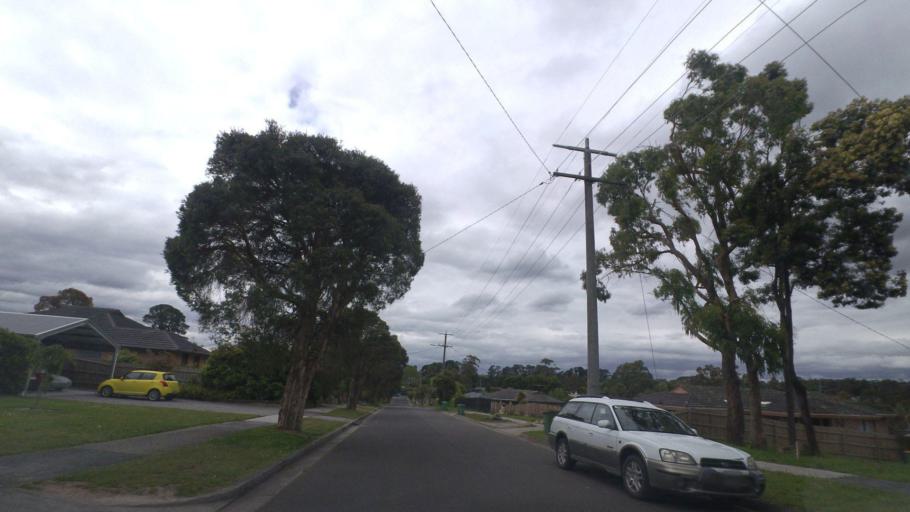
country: AU
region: Victoria
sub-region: Yarra Ranges
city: Mount Evelyn
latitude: -37.7892
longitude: 145.3710
